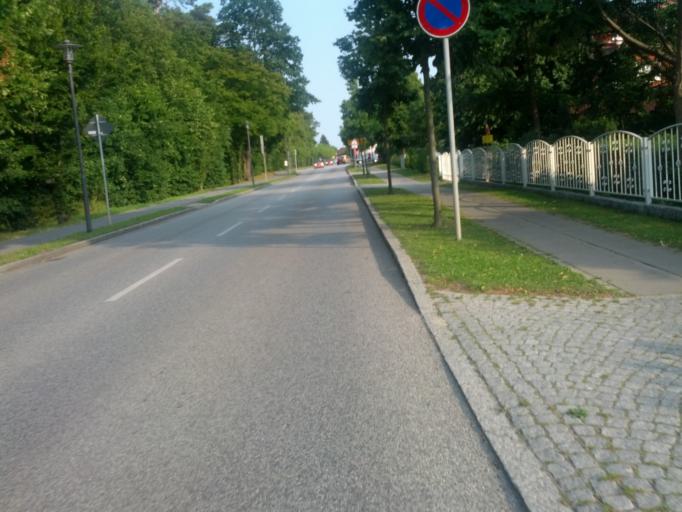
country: DE
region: Mecklenburg-Vorpommern
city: Ostseebad Kuhlungsborn
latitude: 54.1460
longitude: 11.7336
